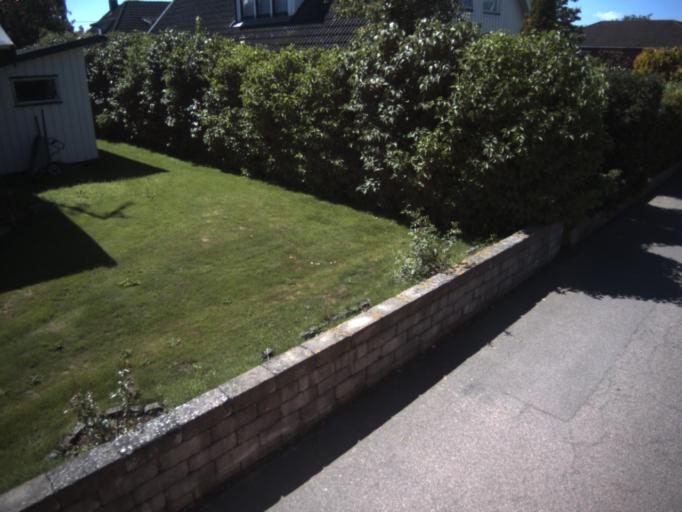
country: SE
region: Skane
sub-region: Helsingborg
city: Glumslov
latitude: 55.9598
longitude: 12.8568
